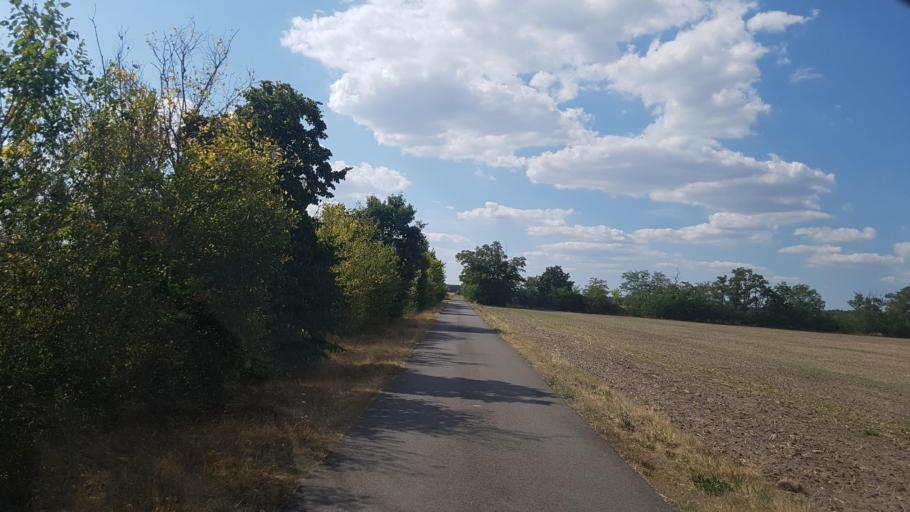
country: DE
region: Saxony-Anhalt
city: Elster
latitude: 51.8368
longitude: 12.8239
